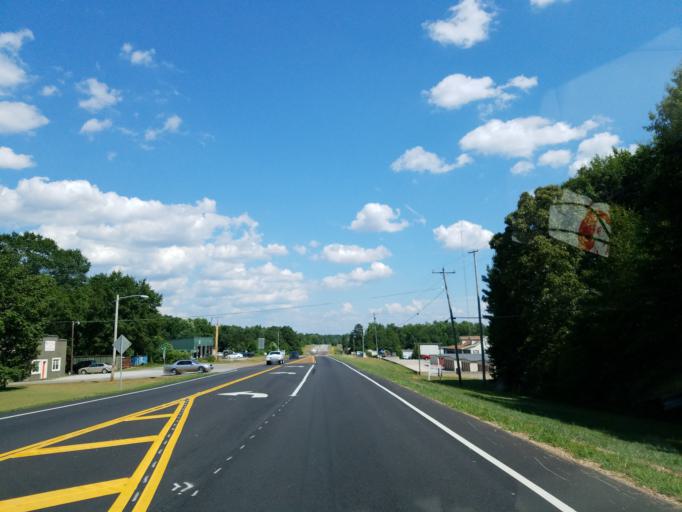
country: US
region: Georgia
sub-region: Lamar County
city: Barnesville
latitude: 33.0346
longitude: -84.1503
